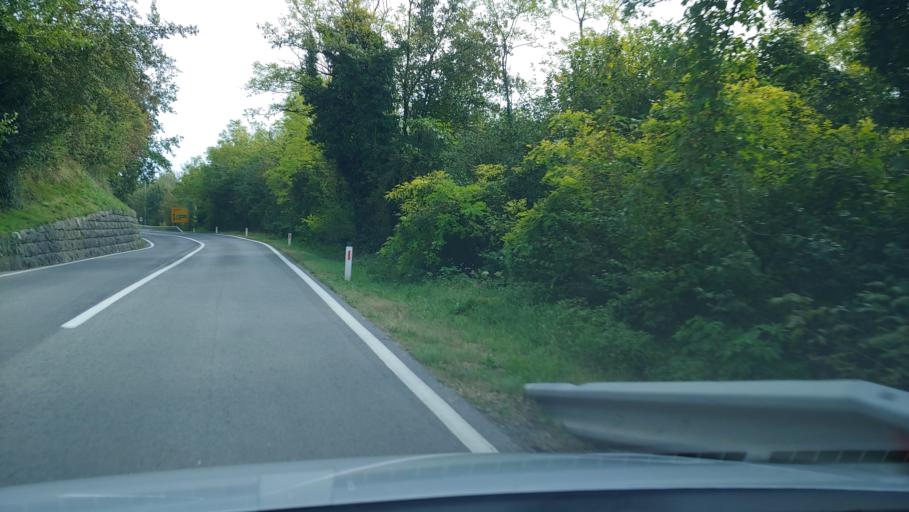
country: SI
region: Nova Gorica
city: Sempas
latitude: 45.8986
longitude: 13.7840
